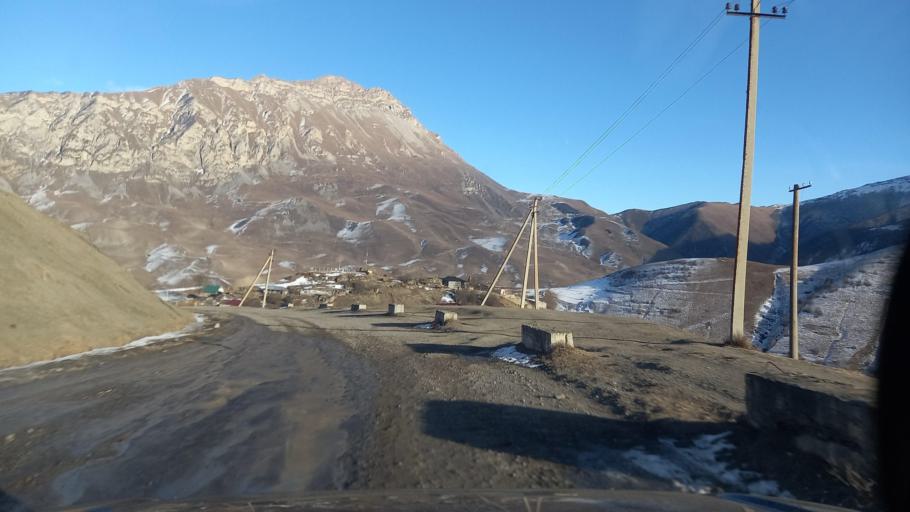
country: RU
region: Ingushetiya
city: Dzhayrakh
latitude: 42.8416
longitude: 44.5043
